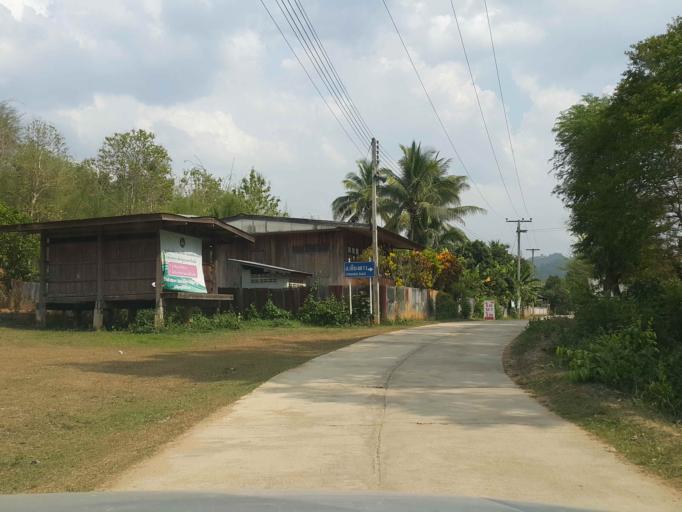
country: TH
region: Chiang Mai
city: Wiang Haeng
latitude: 19.3919
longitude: 98.7224
